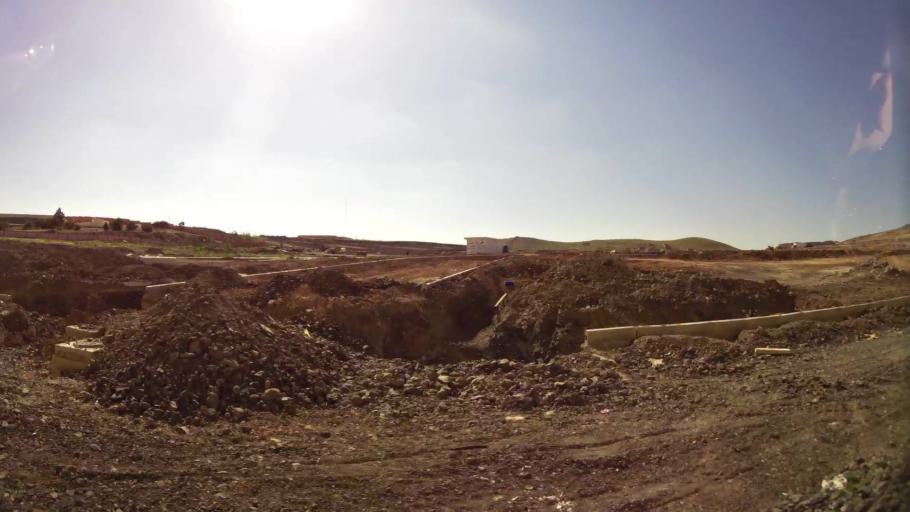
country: MA
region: Oriental
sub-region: Oujda-Angad
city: Oujda
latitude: 34.6503
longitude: -1.9546
